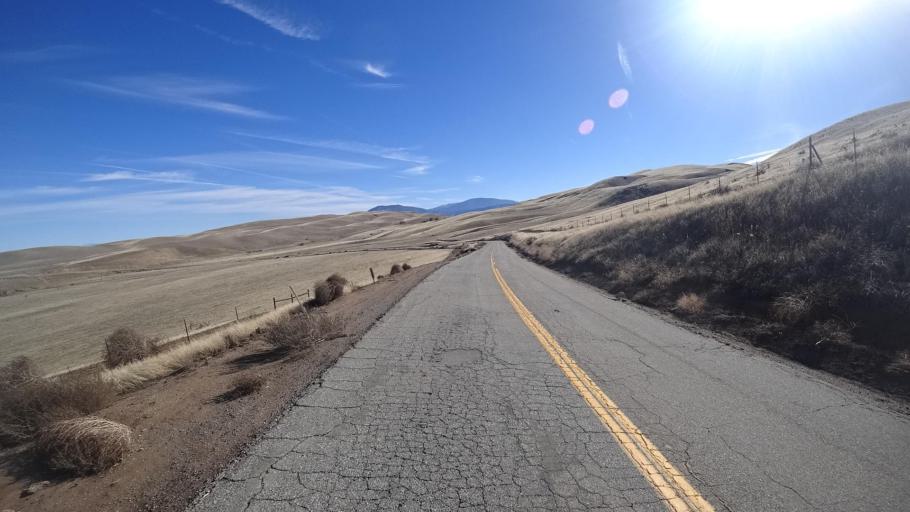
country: US
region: California
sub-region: Kern County
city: Maricopa
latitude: 34.9348
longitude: -119.4087
